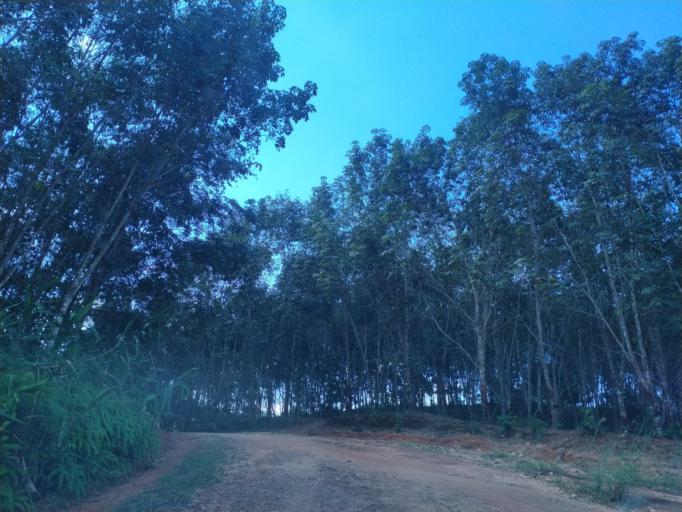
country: LA
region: Vientiane
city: Muang Phon-Hong
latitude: 18.6402
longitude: 102.8869
